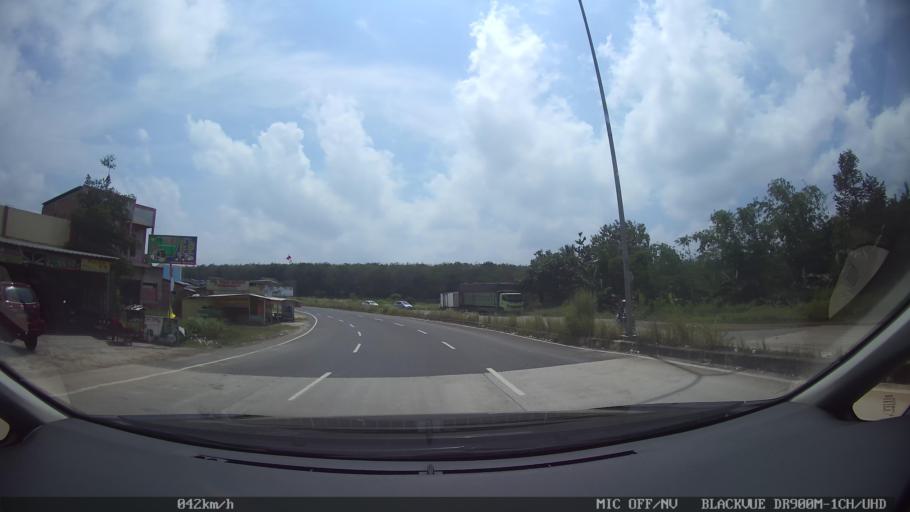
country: ID
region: Lampung
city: Kedaton
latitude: -5.3523
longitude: 105.3246
